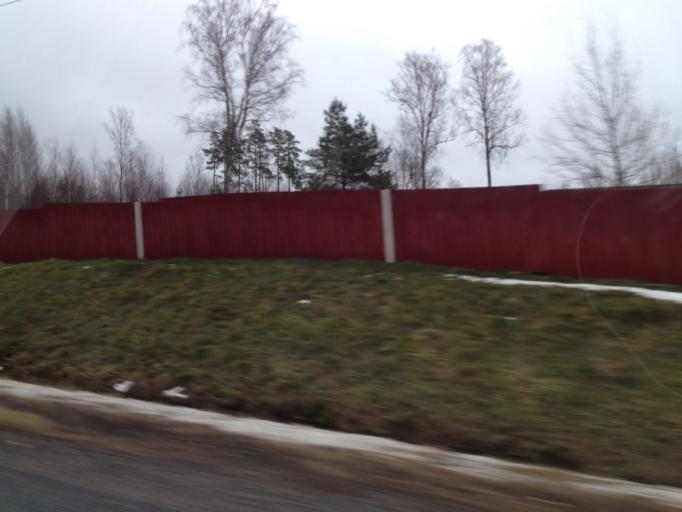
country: FI
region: Uusimaa
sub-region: Raaseporin
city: Ekenaes
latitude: 59.9507
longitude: 23.3588
